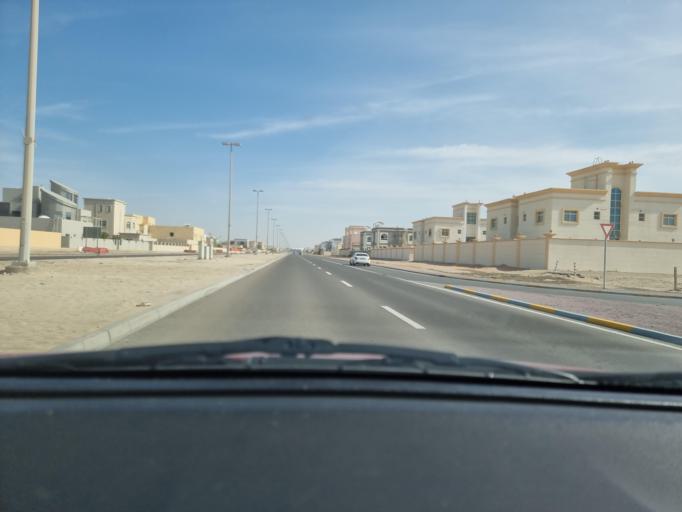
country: AE
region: Abu Dhabi
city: Abu Dhabi
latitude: 24.3162
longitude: 54.5655
